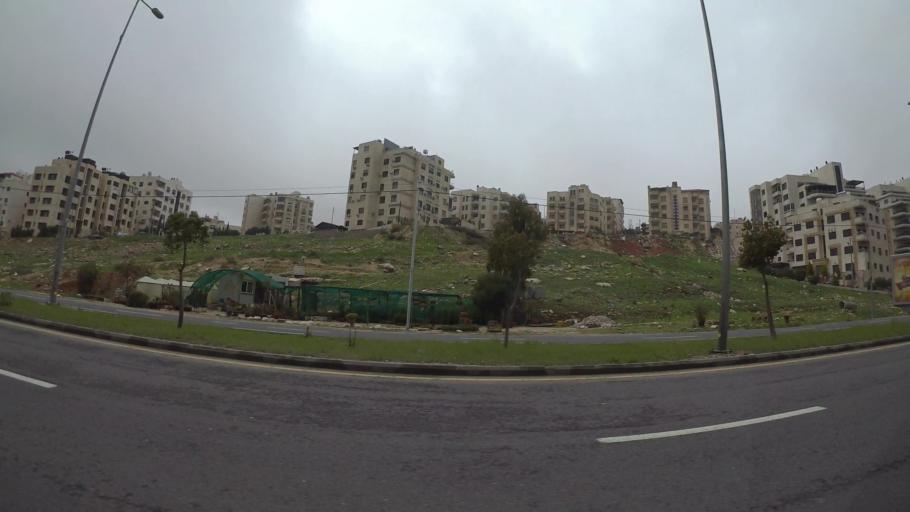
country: JO
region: Amman
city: Al Bunayyat ash Shamaliyah
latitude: 31.9373
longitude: 35.8718
